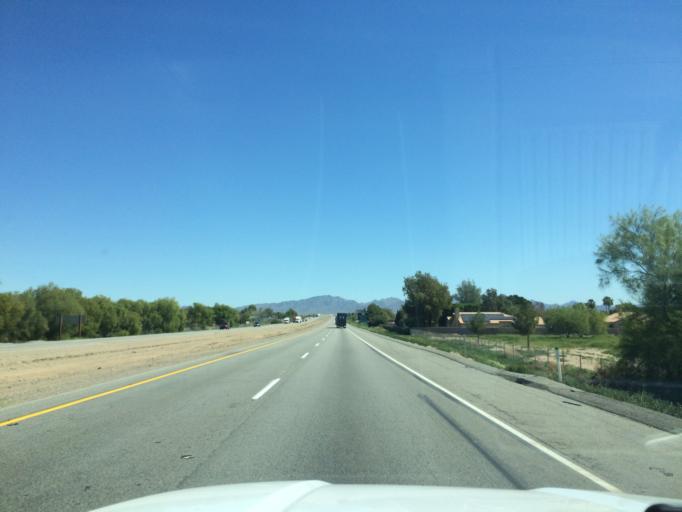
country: US
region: California
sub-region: Riverside County
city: Blythe
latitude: 33.6071
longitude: -114.5828
